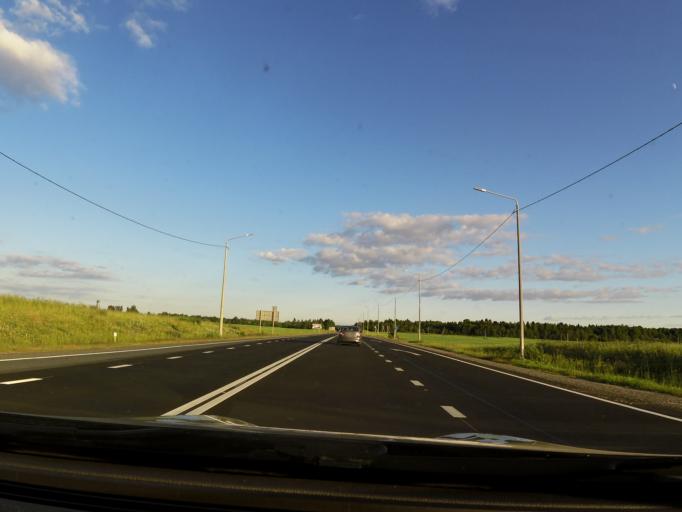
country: RU
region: Vologda
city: Gryazovets
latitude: 59.0192
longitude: 40.1167
